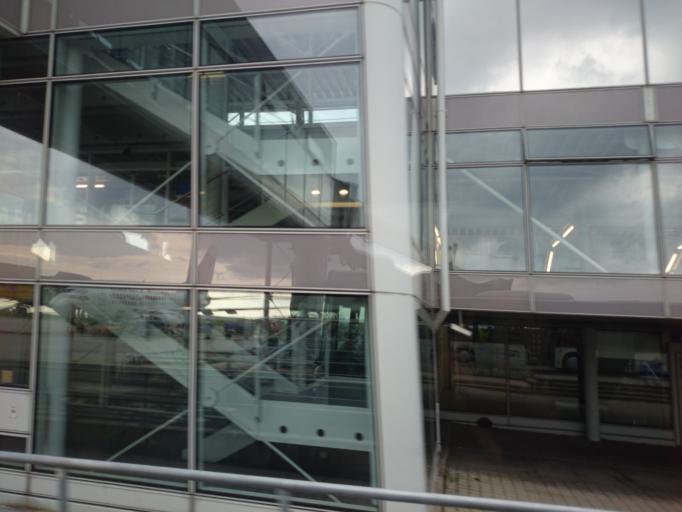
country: DE
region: Saxony
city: Schkeuditz
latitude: 51.4191
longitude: 12.2220
